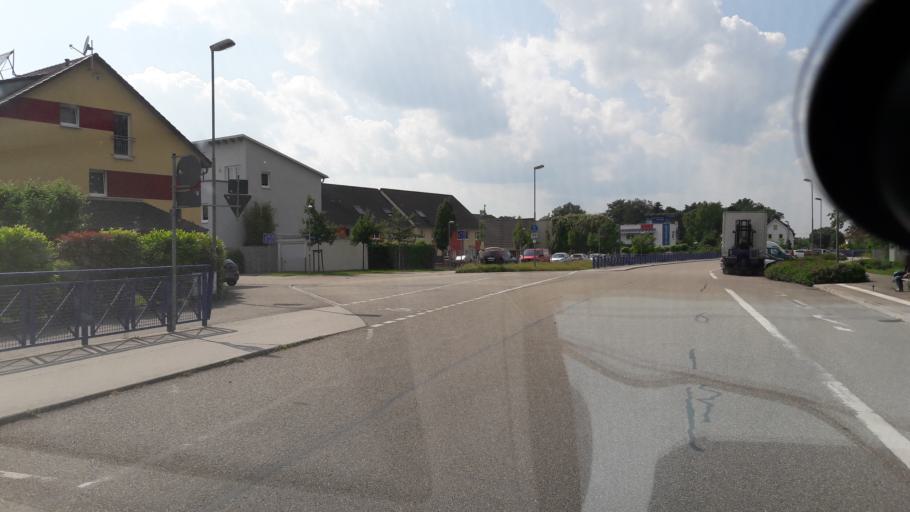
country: DE
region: Baden-Wuerttemberg
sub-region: Karlsruhe Region
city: Rheinstetten
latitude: 48.9626
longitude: 8.3393
